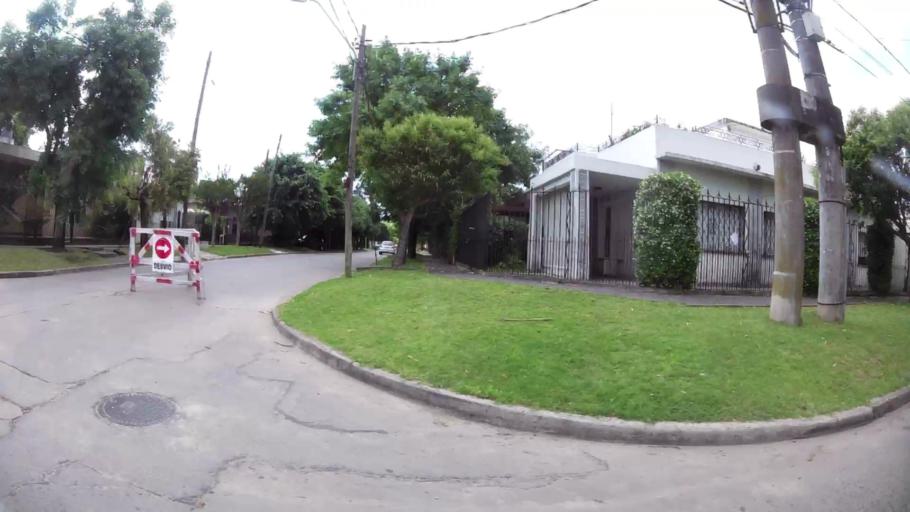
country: AR
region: Buenos Aires
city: Ituzaingo
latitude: -34.6470
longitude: -58.6608
